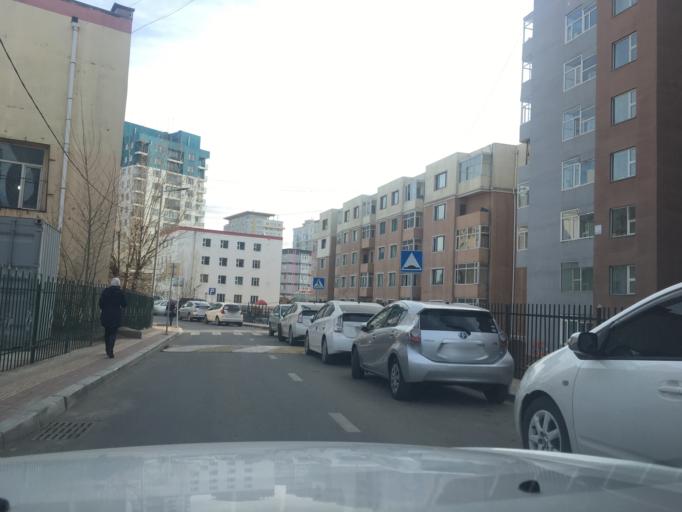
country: MN
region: Ulaanbaatar
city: Ulaanbaatar
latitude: 47.9169
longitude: 106.8871
